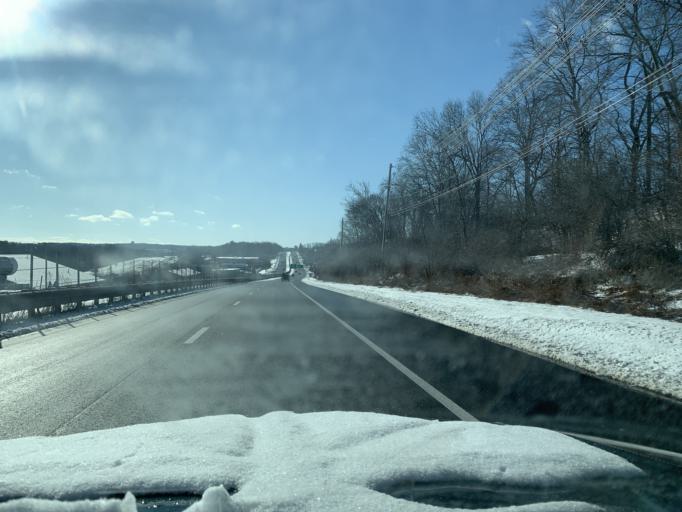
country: US
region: Massachusetts
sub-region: Essex County
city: Danvers
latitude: 42.5786
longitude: -70.9695
